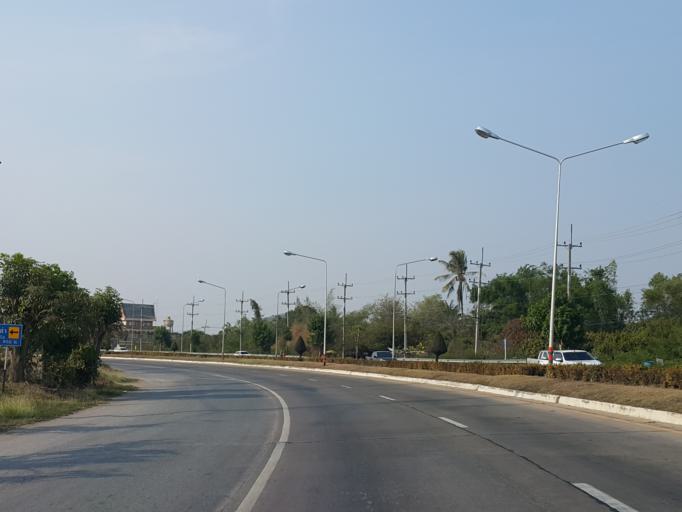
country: TH
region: Suphan Buri
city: Doembang Nangbuat
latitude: 14.8109
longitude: 100.1187
